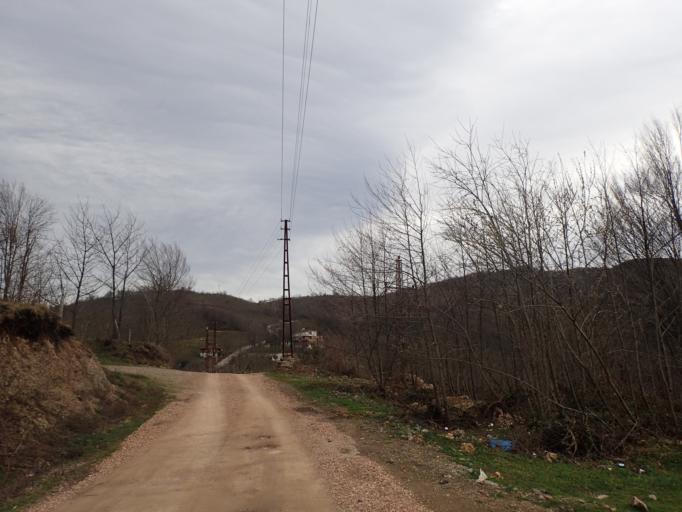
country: TR
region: Ordu
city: Camas
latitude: 40.8896
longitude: 37.5226
